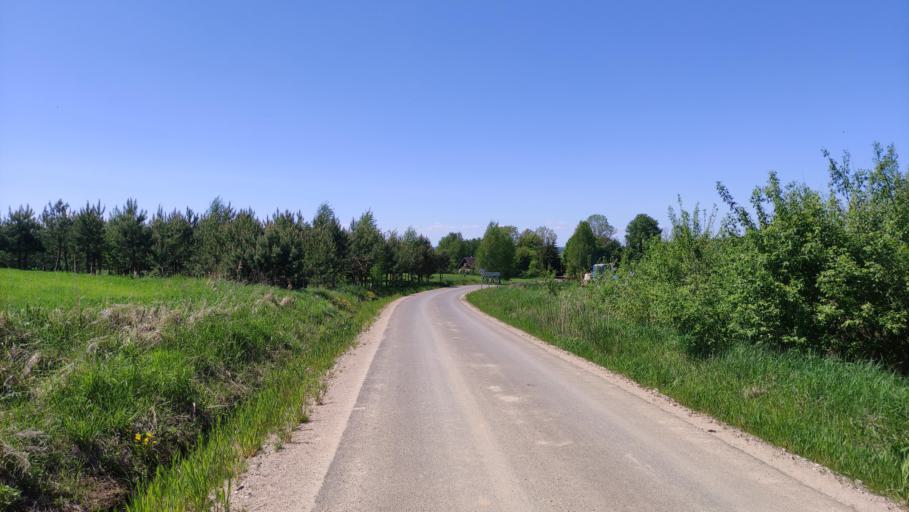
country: LT
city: Simnas
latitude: 54.3136
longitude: 23.7955
